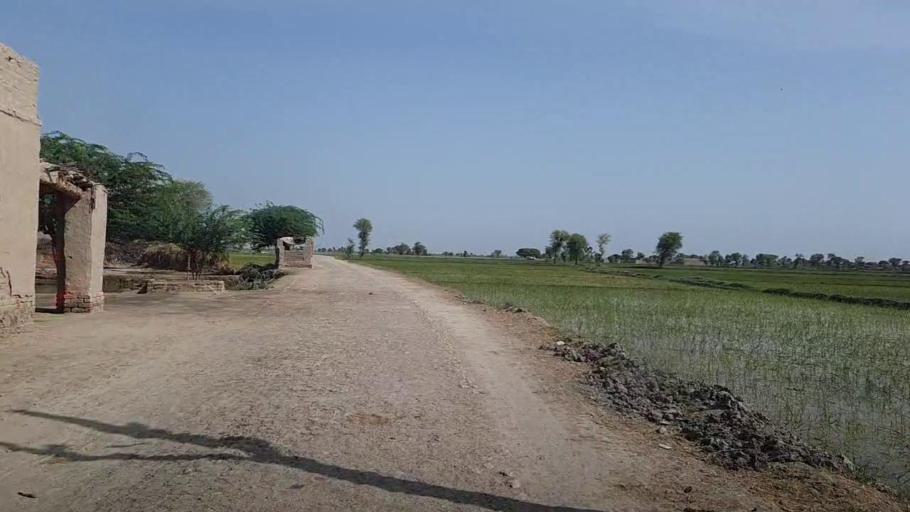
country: PK
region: Sindh
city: Mehar
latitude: 27.1162
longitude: 67.8430
